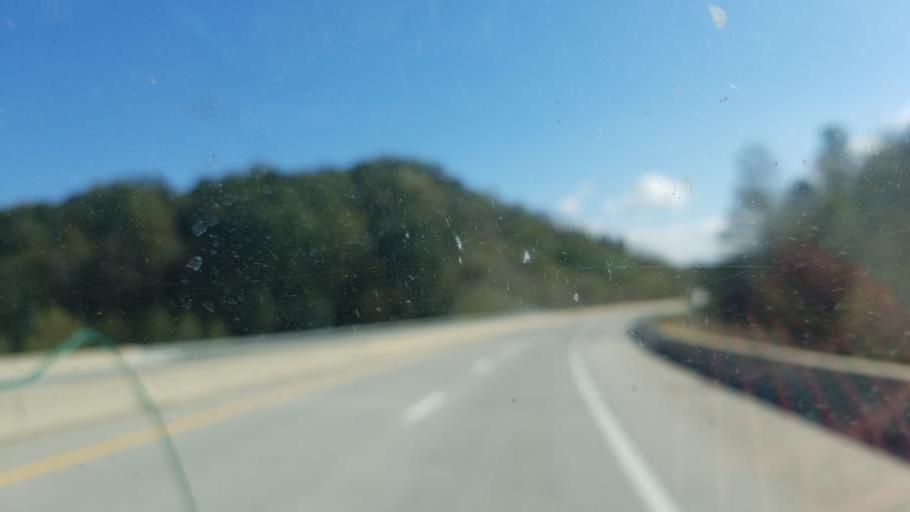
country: US
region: Pennsylvania
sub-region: Bedford County
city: Everett
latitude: 40.0275
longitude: -78.3730
